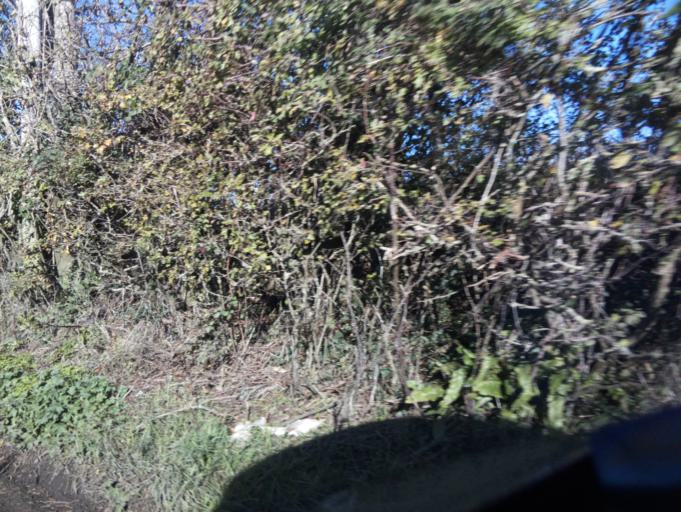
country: GB
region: England
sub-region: Somerset
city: Ilchester
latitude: 50.9696
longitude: -2.7006
